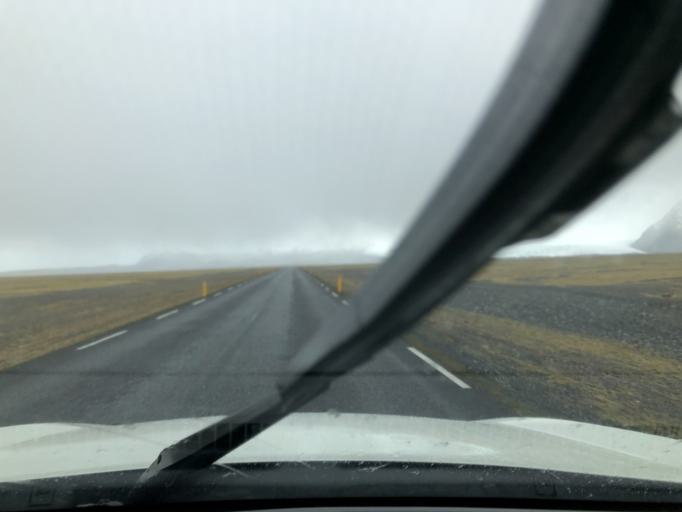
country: IS
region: East
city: Hoefn
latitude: 64.0317
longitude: -16.3009
